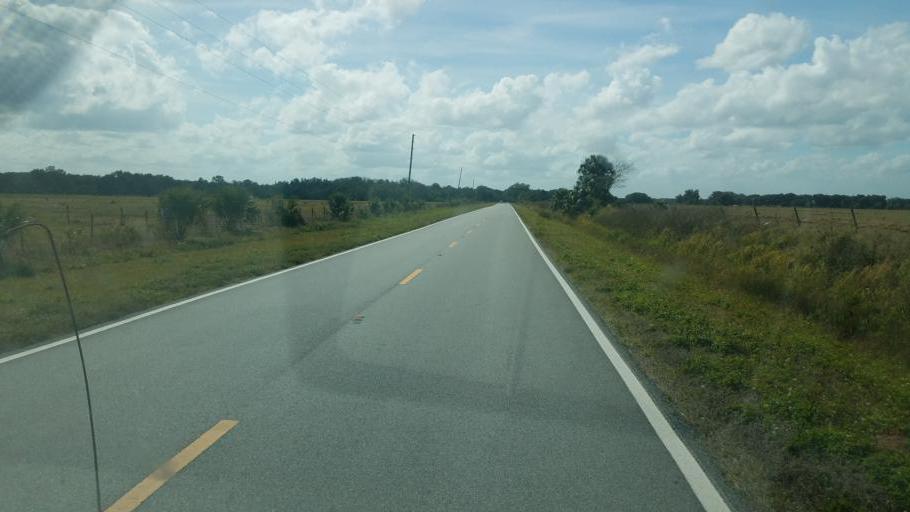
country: US
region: Florida
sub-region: Polk County
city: Babson Park
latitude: 27.9630
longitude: -81.4088
